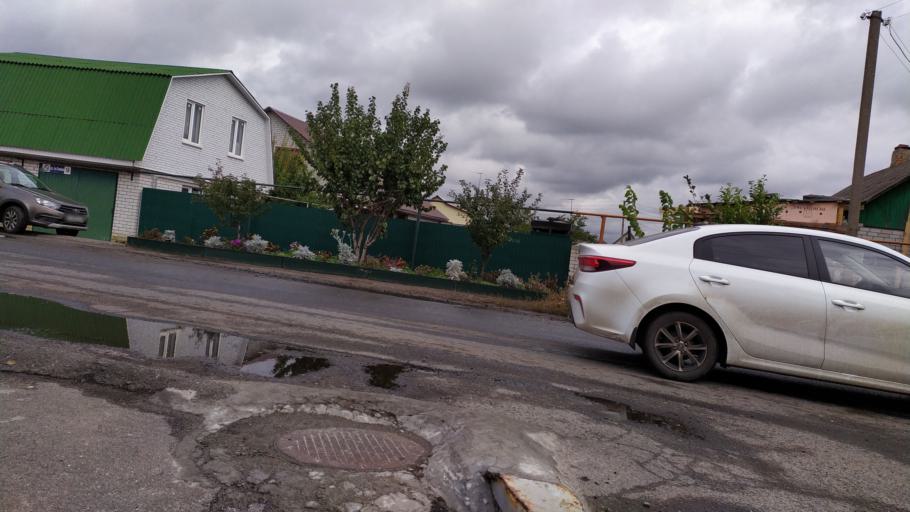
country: RU
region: Kursk
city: Kursk
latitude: 51.6445
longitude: 36.1478
